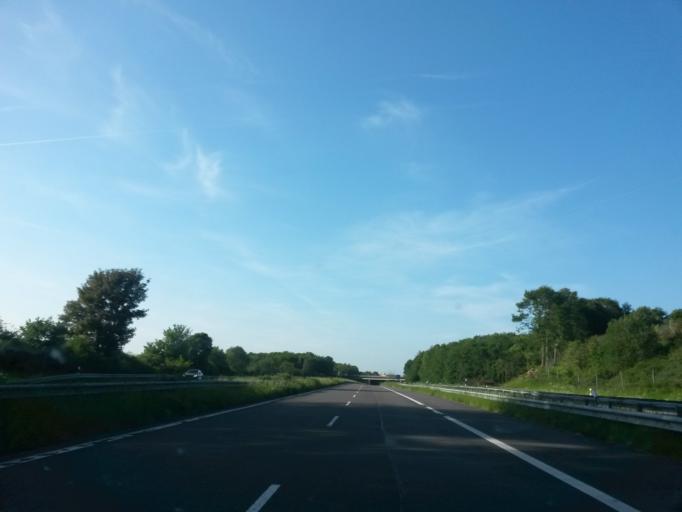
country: DE
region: North Rhine-Westphalia
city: Bergneustadt
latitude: 50.9721
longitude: 7.6422
